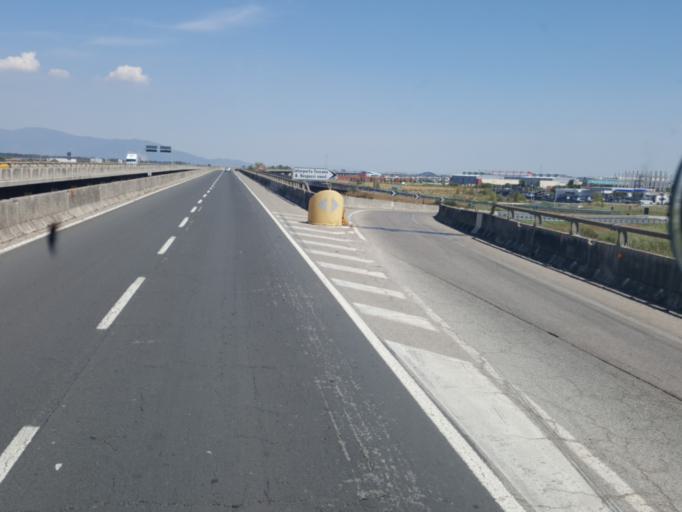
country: IT
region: Tuscany
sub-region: Provincia di Livorno
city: Guasticce
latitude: 43.6003
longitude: 10.3701
